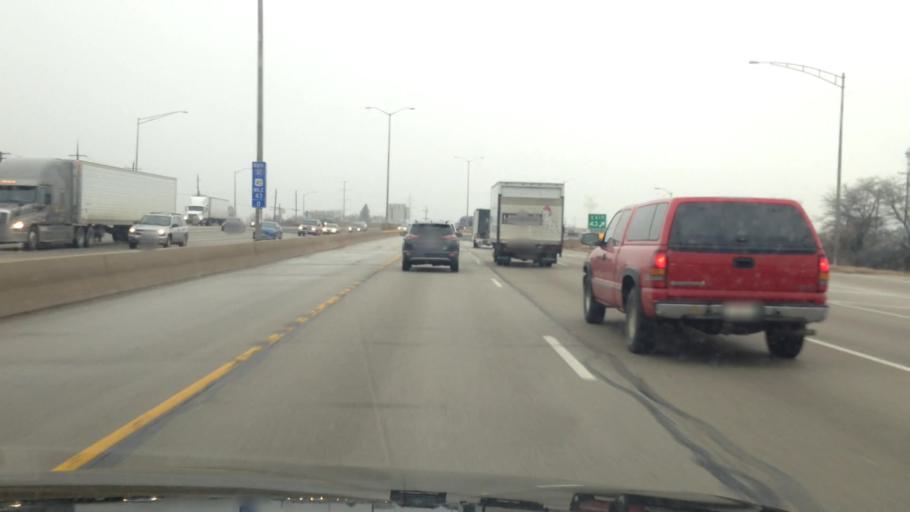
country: US
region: Wisconsin
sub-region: Waukesha County
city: Elm Grove
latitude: 43.0714
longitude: -88.0562
